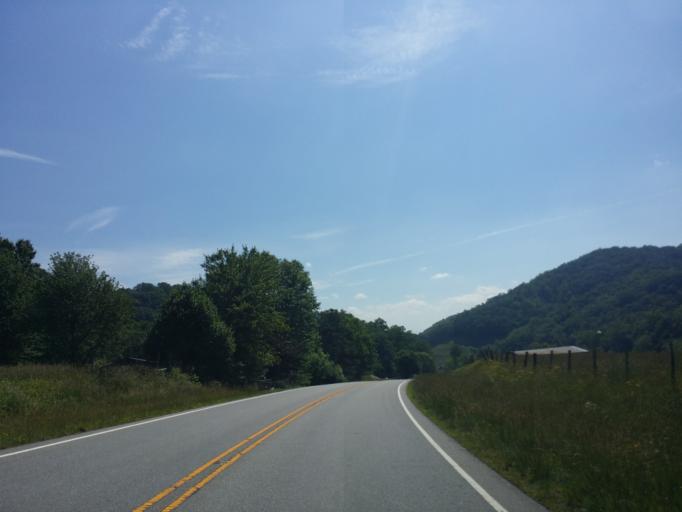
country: US
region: North Carolina
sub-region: Madison County
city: Marshall
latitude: 35.6999
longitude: -82.8129
